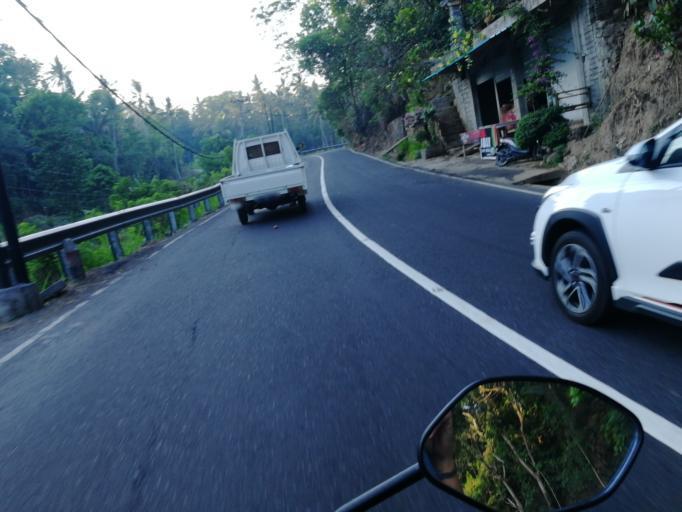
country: ID
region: Bali
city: Tistagede
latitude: -8.3717
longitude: 115.6098
